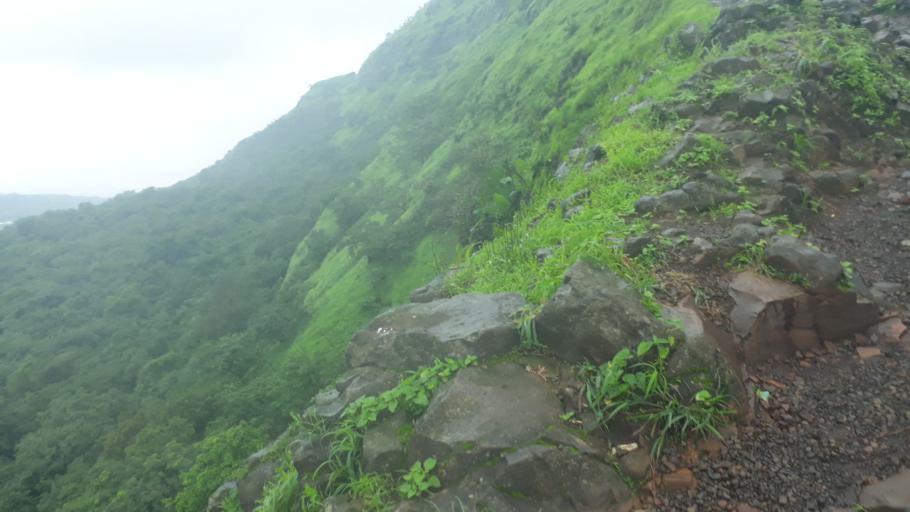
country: IN
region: Maharashtra
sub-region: Pune Division
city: Wadgaon
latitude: 18.6313
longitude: 73.5176
